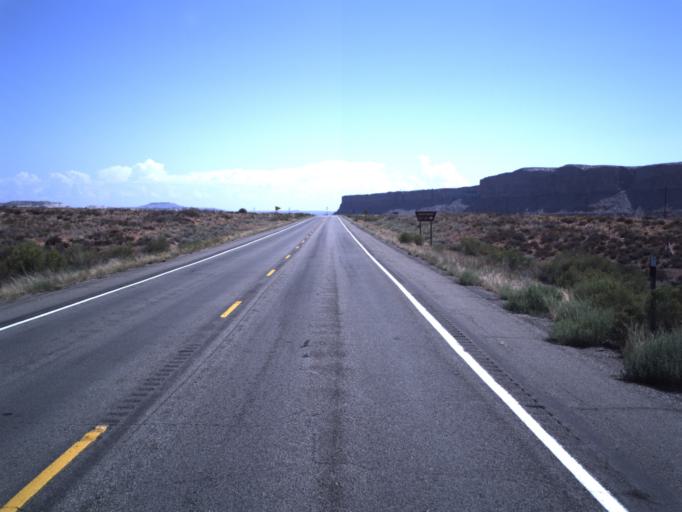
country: US
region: Utah
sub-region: San Juan County
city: Blanding
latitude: 37.2665
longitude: -109.6152
